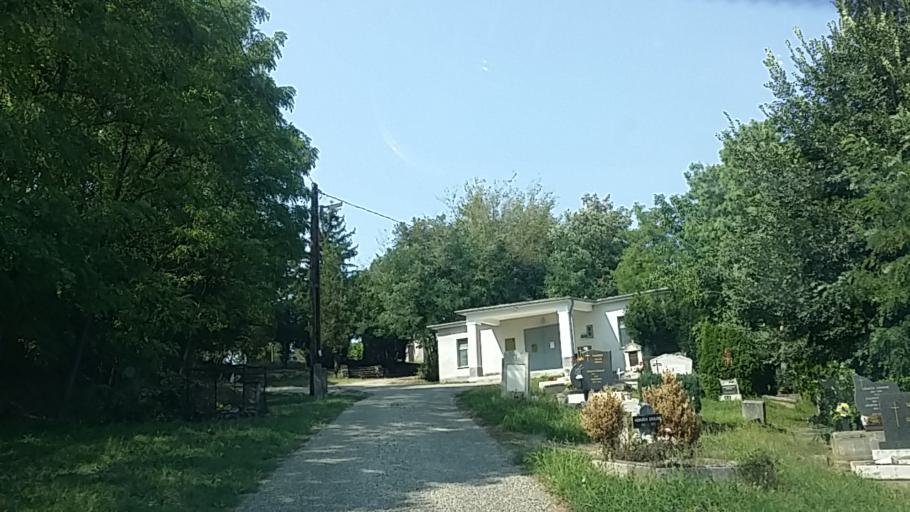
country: HU
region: Gyor-Moson-Sopron
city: Nagycenk
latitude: 47.6546
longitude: 16.6639
